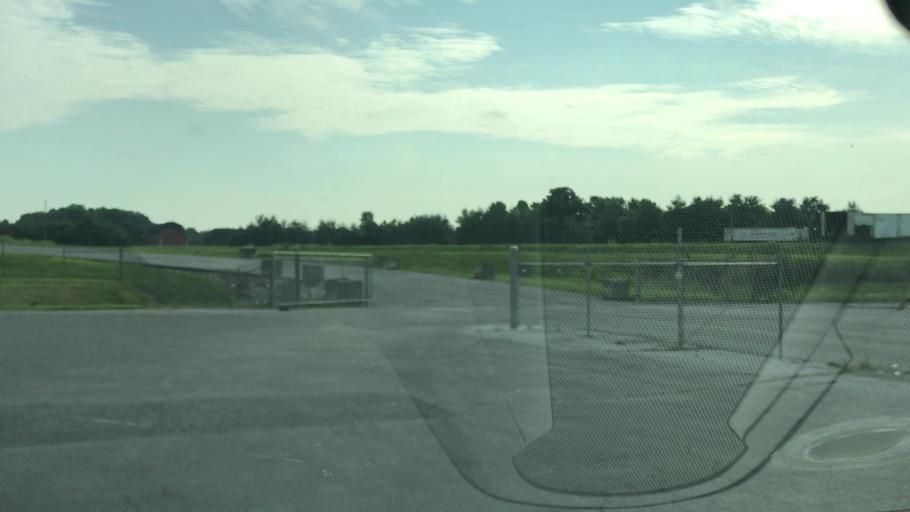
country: US
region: Pennsylvania
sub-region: Franklin County
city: State Line
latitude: 39.7169
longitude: -77.7205
